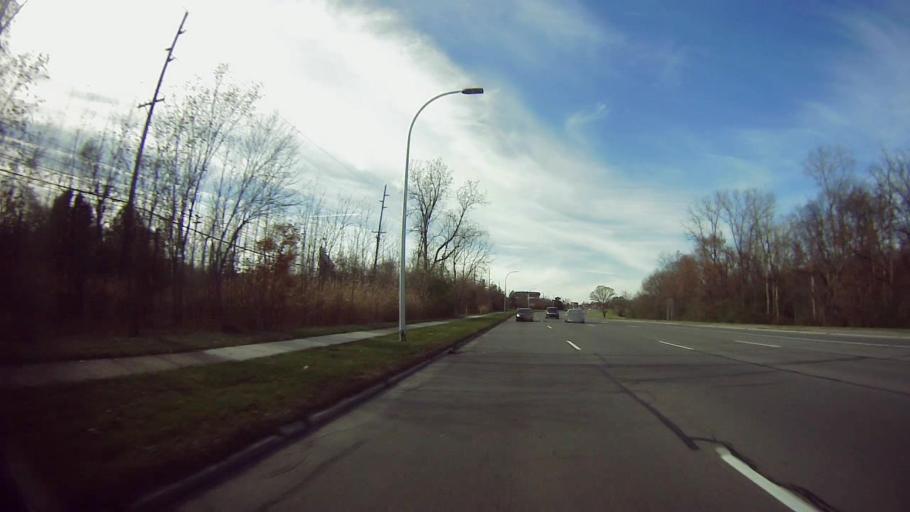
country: US
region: Michigan
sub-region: Wayne County
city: Allen Park
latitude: 42.3081
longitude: -83.2280
